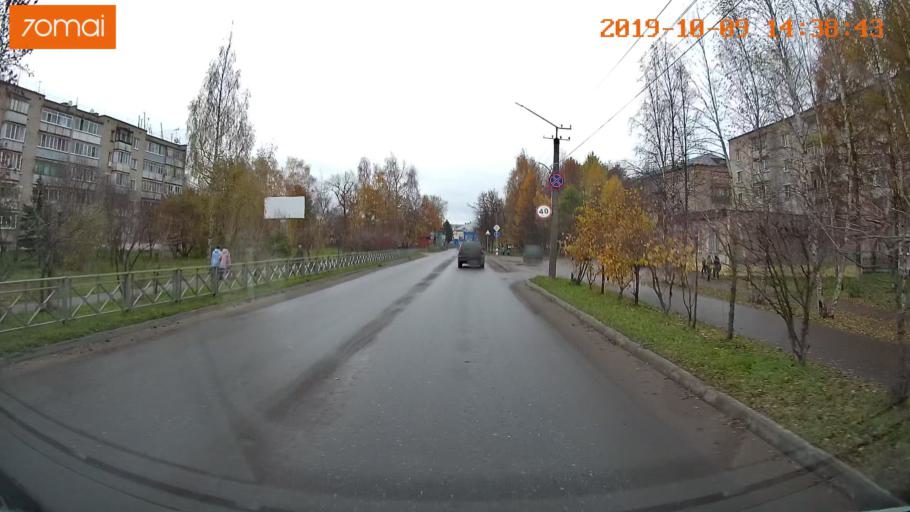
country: RU
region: Kostroma
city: Buy
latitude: 58.4791
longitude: 41.5364
